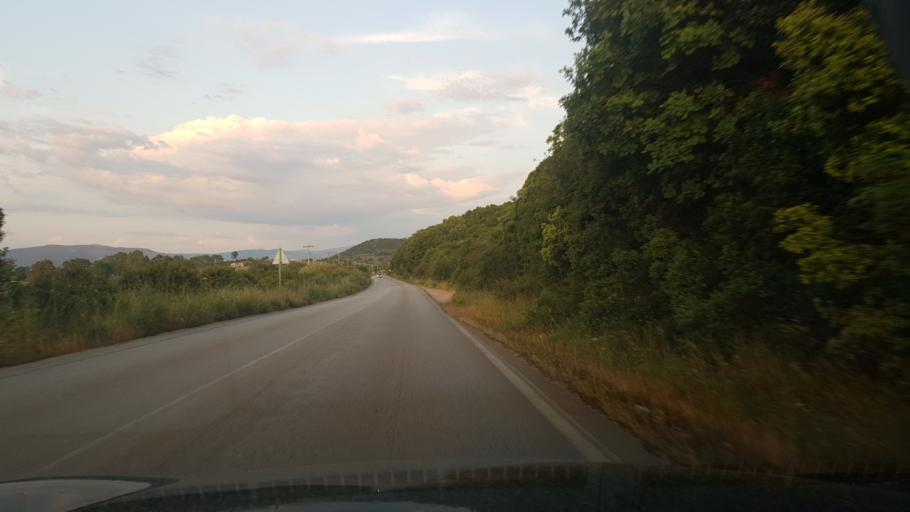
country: GR
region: Ionian Islands
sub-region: Lefkada
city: Lefkada
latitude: 38.8635
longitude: 20.7825
